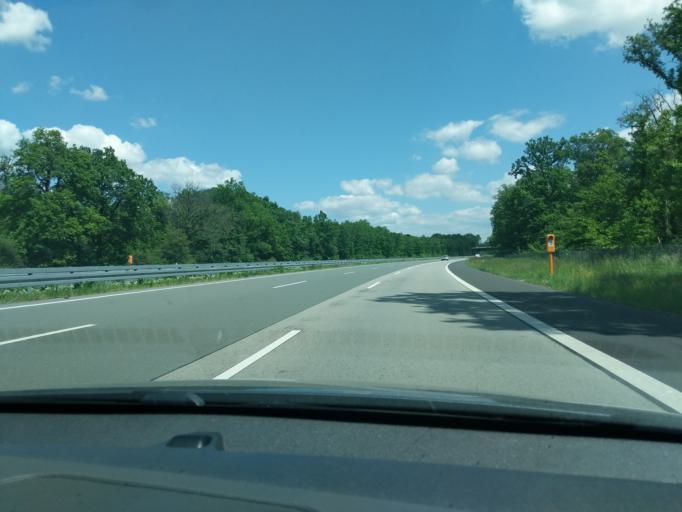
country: DE
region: Hesse
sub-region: Regierungsbezirk Darmstadt
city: Offenbach
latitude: 50.1435
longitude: 8.7779
